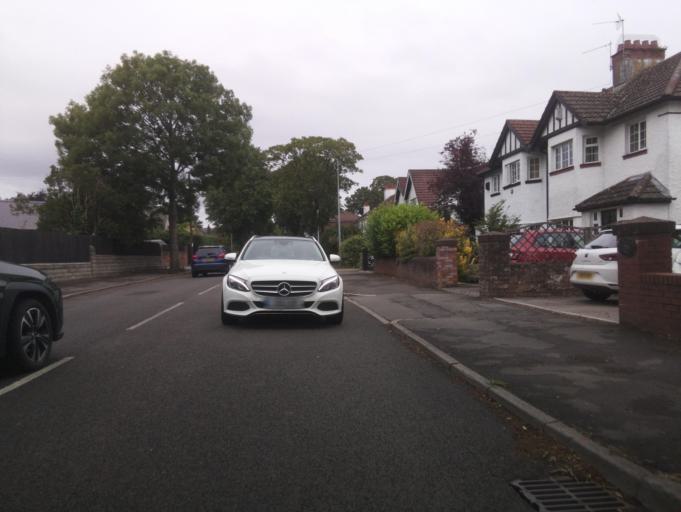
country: GB
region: Wales
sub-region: Vale of Glamorgan
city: Penarth
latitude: 51.4233
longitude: -3.1763
